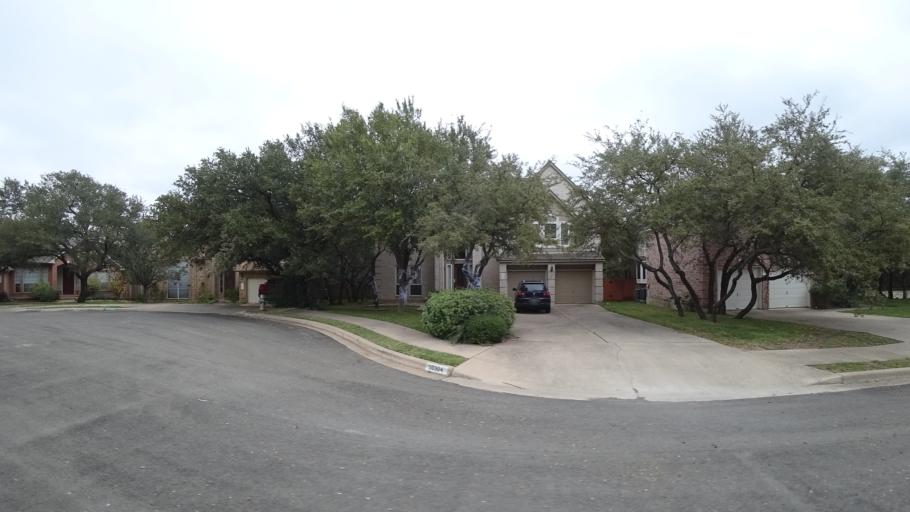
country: US
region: Texas
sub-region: Williamson County
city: Anderson Mill
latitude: 30.4388
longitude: -97.8281
